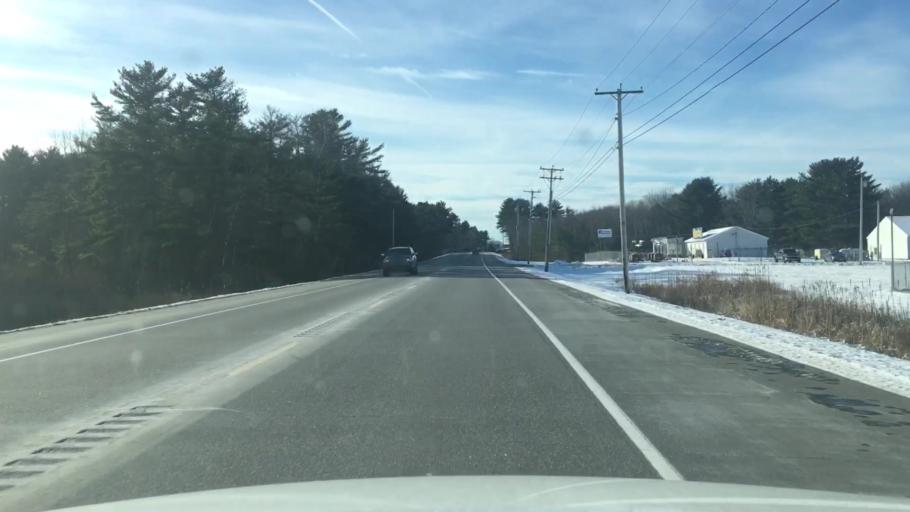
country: US
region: Maine
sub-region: Sagadahoc County
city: Woolwich
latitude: 43.9307
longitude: -69.7845
